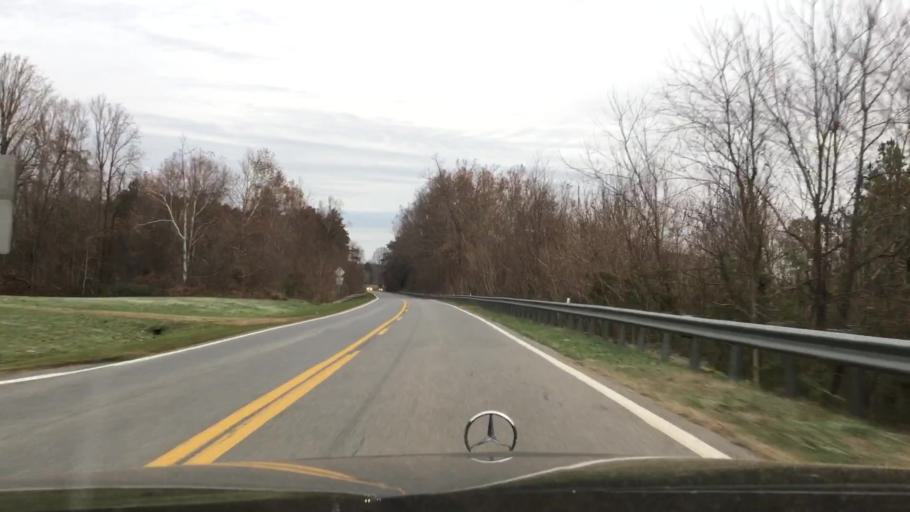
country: US
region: Virginia
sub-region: Campbell County
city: Altavista
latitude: 37.1575
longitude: -79.2974
